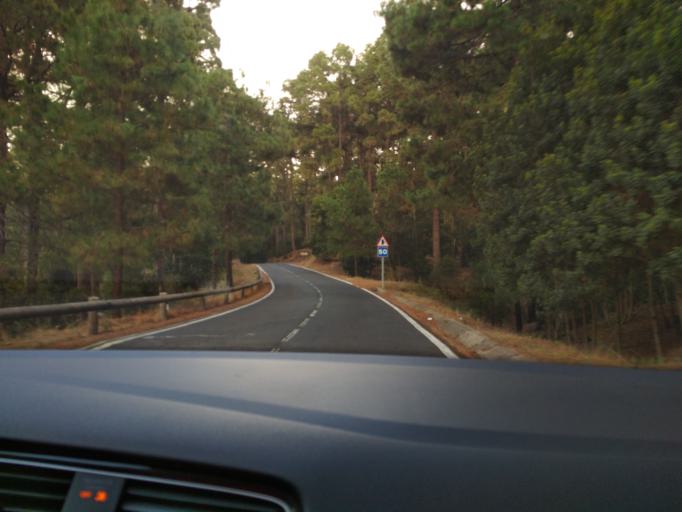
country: ES
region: Canary Islands
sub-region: Provincia de Santa Cruz de Tenerife
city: Garachico
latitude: 28.3327
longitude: -16.7596
